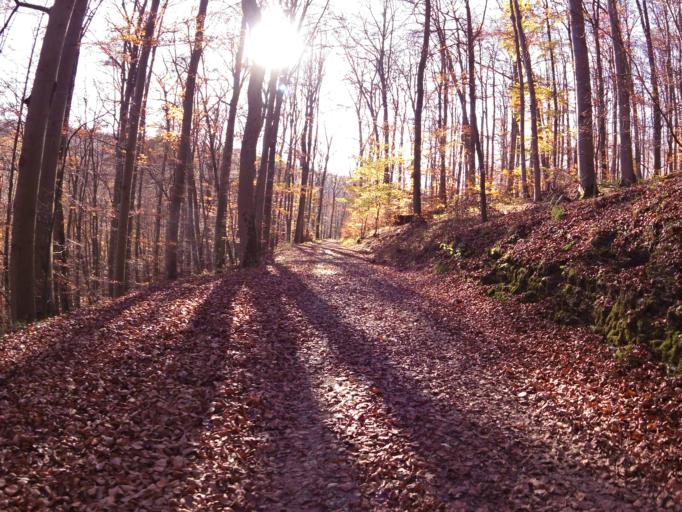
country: DE
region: Thuringia
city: Kammerforst
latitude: 51.0700
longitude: 10.4351
